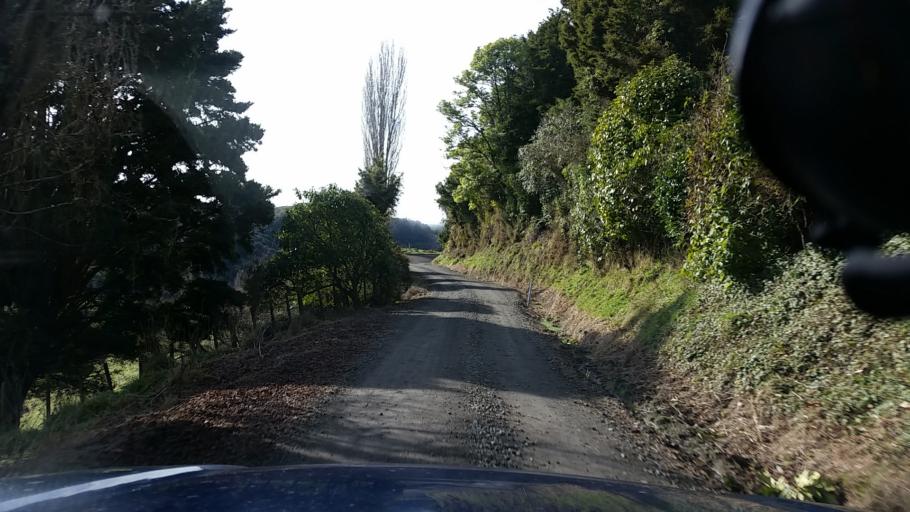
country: NZ
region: Taranaki
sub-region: New Plymouth District
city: Waitara
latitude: -39.0327
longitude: 174.7877
